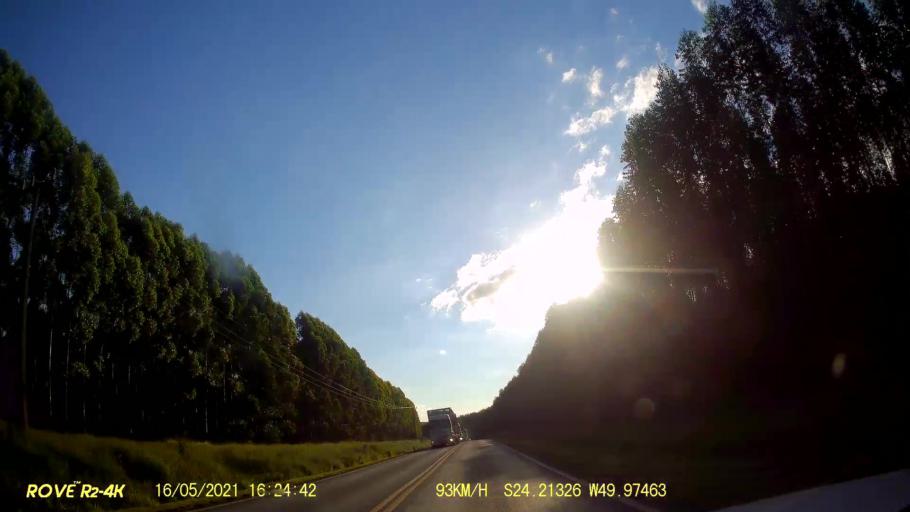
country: BR
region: Parana
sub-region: Jaguariaiva
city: Jaguariaiva
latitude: -24.2132
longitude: -49.9750
